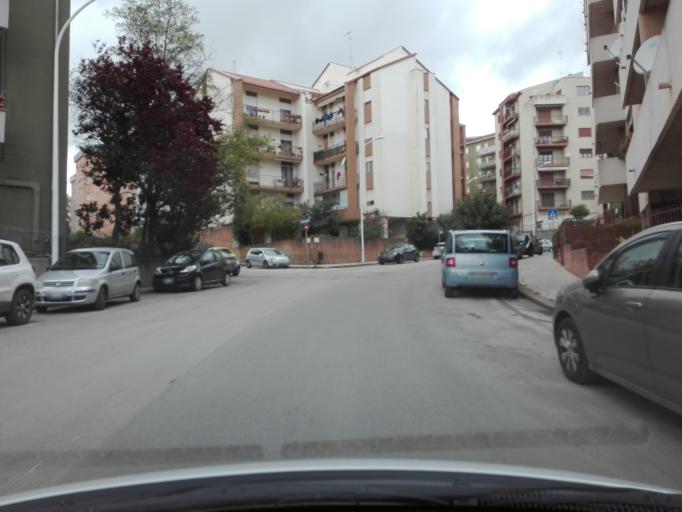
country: IT
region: Sardinia
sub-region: Provincia di Sassari
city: Sassari
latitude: 40.7267
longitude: 8.5790
